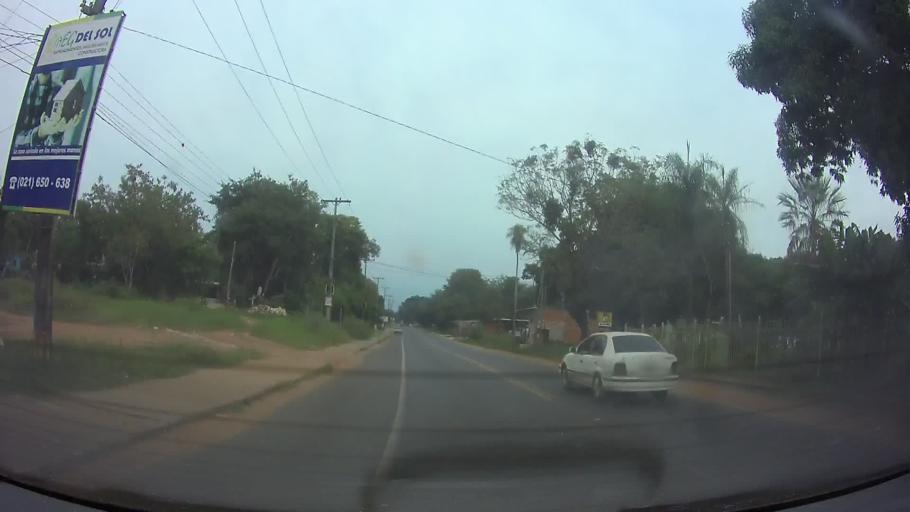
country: PY
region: Central
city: Limpio
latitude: -25.2360
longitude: -57.4508
